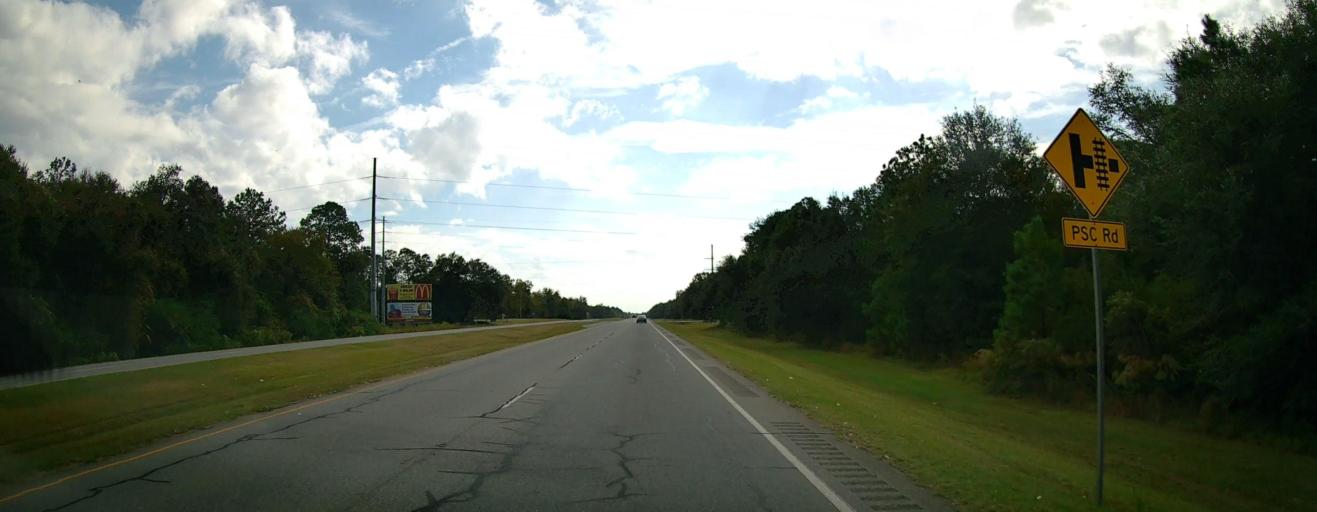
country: US
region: Georgia
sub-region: Mitchell County
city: Camilla
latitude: 31.2632
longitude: -84.1947
